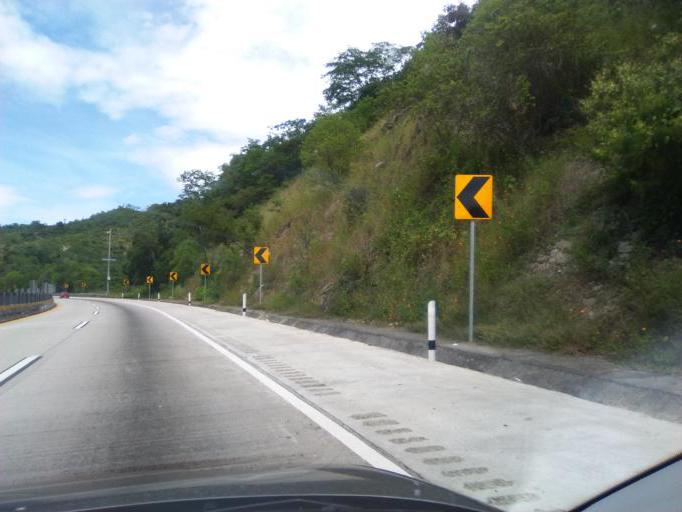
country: MX
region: Guerrero
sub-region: Chilpancingo de los Bravo
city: Julian Blanco (Dos Caminos)
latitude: 17.1976
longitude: -99.5322
